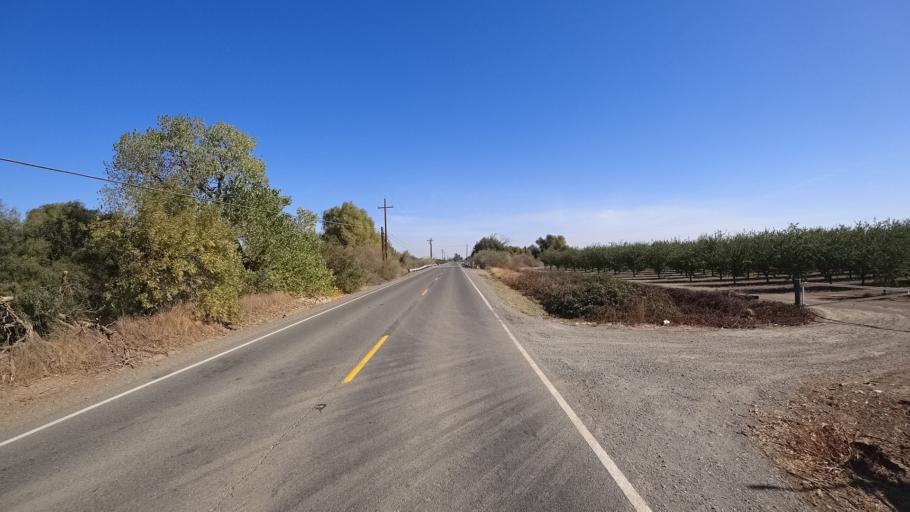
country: US
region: California
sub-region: Yolo County
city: Woodland
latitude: 38.6196
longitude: -121.8337
